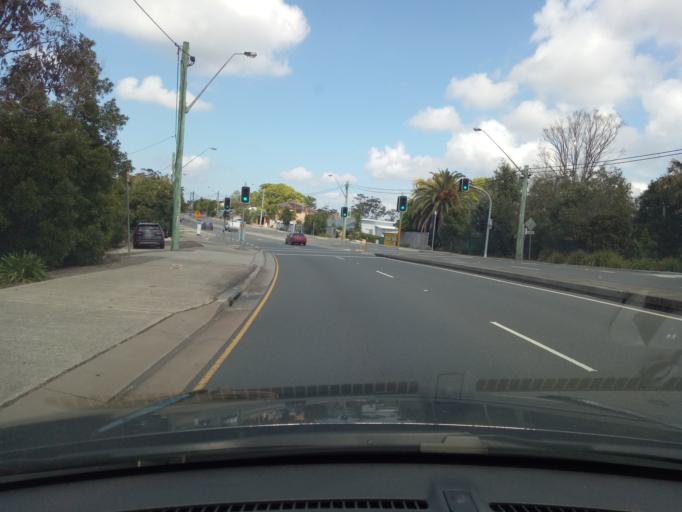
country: AU
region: New South Wales
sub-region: Gosford Shire
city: Holgate
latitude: -33.4199
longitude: 151.4397
